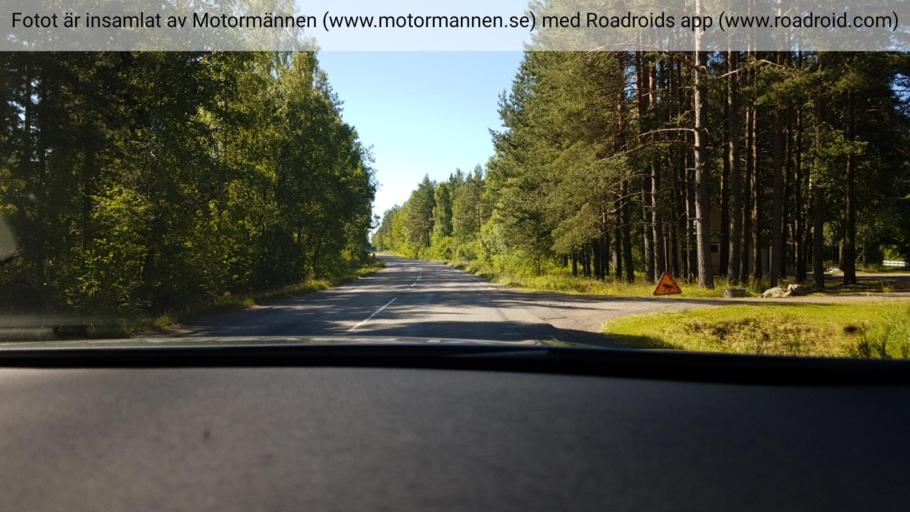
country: SE
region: Vaestra Goetaland
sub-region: Tidaholms Kommun
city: Tidaholm
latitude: 58.1618
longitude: 13.9622
